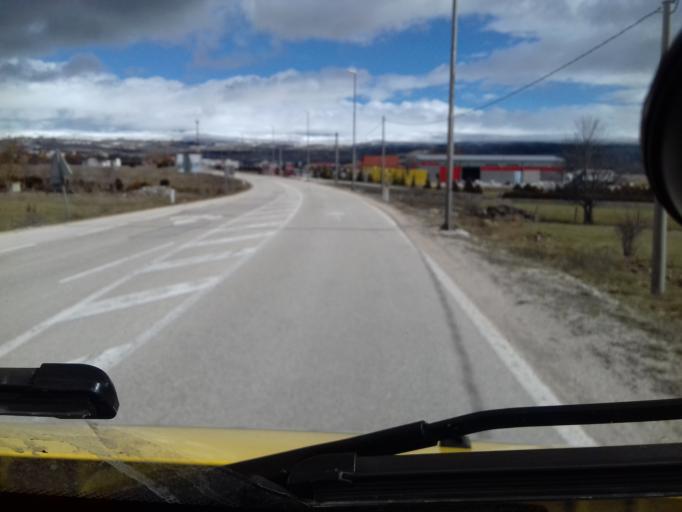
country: BA
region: Federation of Bosnia and Herzegovina
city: Tomislavgrad
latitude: 43.7006
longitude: 17.2169
